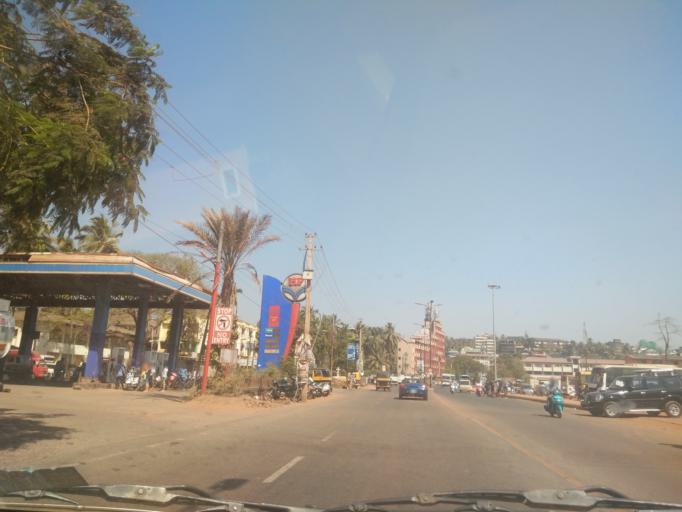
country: IN
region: Goa
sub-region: North Goa
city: Mapuca
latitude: 15.5878
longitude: 73.8087
